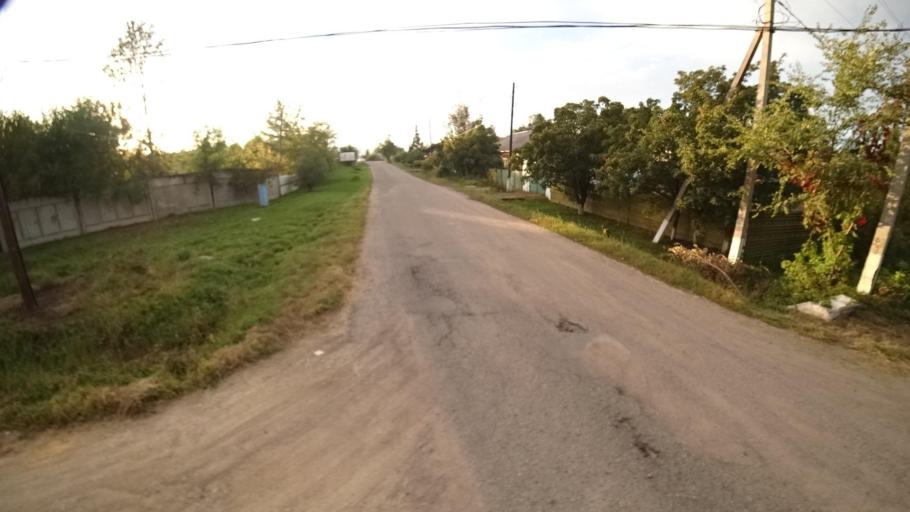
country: RU
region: Primorskiy
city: Yakovlevka
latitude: 44.4263
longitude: 133.4819
